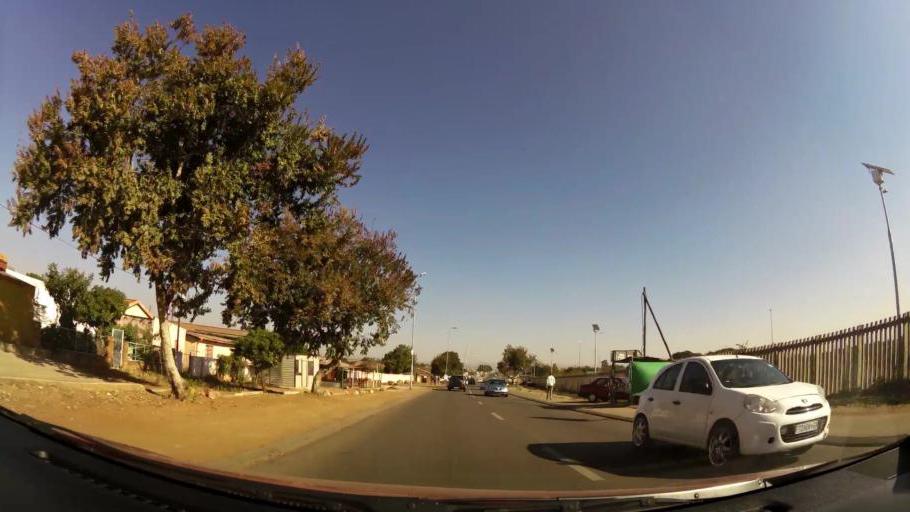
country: ZA
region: Gauteng
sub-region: City of Tshwane Metropolitan Municipality
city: Mabopane
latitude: -25.5454
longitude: 28.0962
